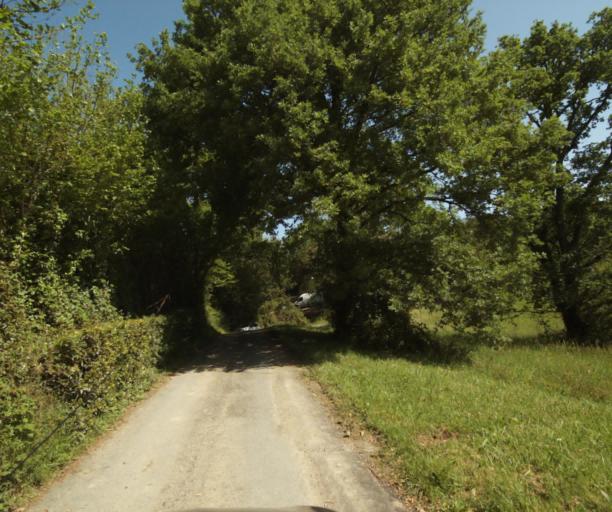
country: FR
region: Aquitaine
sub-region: Departement des Pyrenees-Atlantiques
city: Villefranque
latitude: 43.4530
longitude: -1.4391
